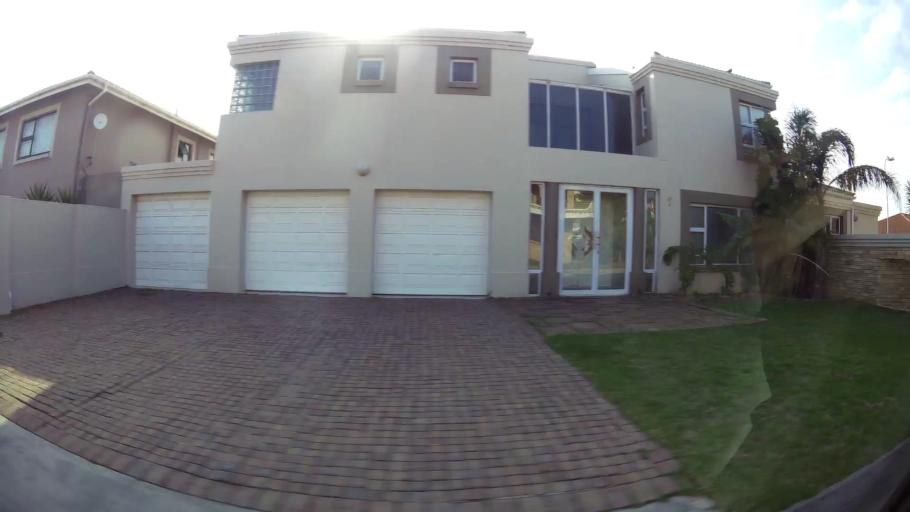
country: ZA
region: Eastern Cape
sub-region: Nelson Mandela Bay Metropolitan Municipality
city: Port Elizabeth
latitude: -33.9255
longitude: 25.5598
